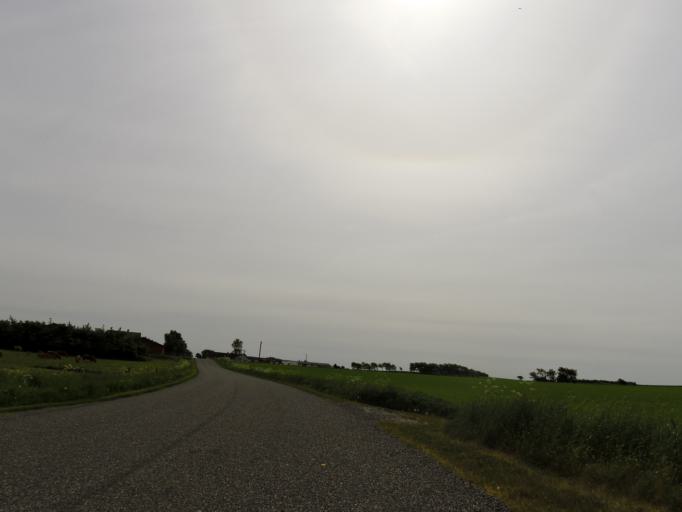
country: DK
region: Central Jutland
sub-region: Holstebro Kommune
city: Vinderup
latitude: 56.5849
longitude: 8.7736
